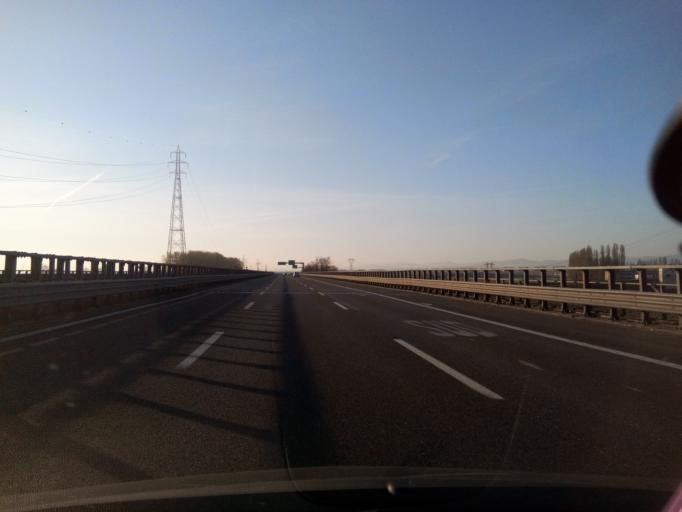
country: IT
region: Emilia-Romagna
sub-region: Provincia di Piacenza
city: Piacenza
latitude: 45.0648
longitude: 9.7352
